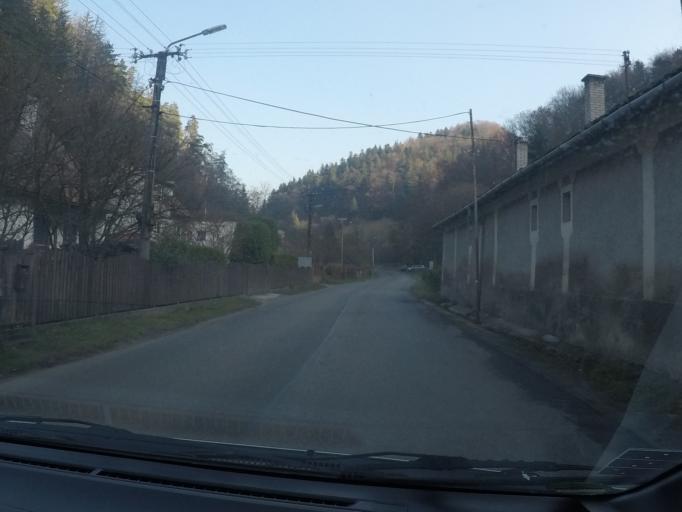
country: SK
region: Banskobystricky
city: Zarnovica
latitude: 48.4533
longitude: 18.7872
